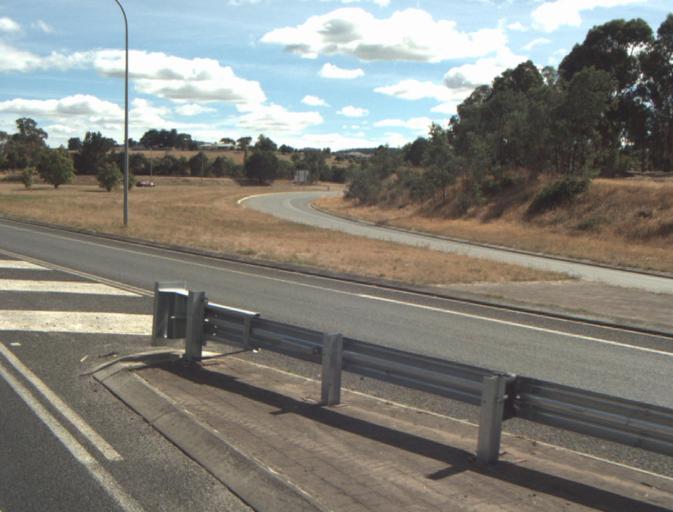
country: AU
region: Tasmania
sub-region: Launceston
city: Newnham
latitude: -41.3999
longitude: 147.1162
